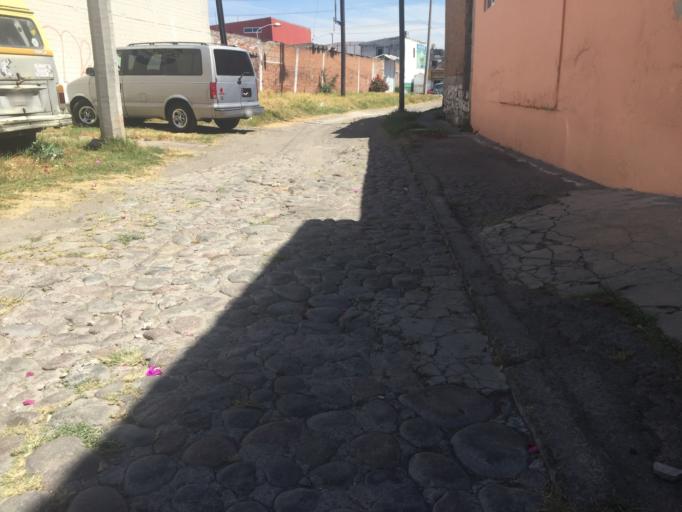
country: MX
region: Puebla
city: Puebla
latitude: 19.0621
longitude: -98.2319
